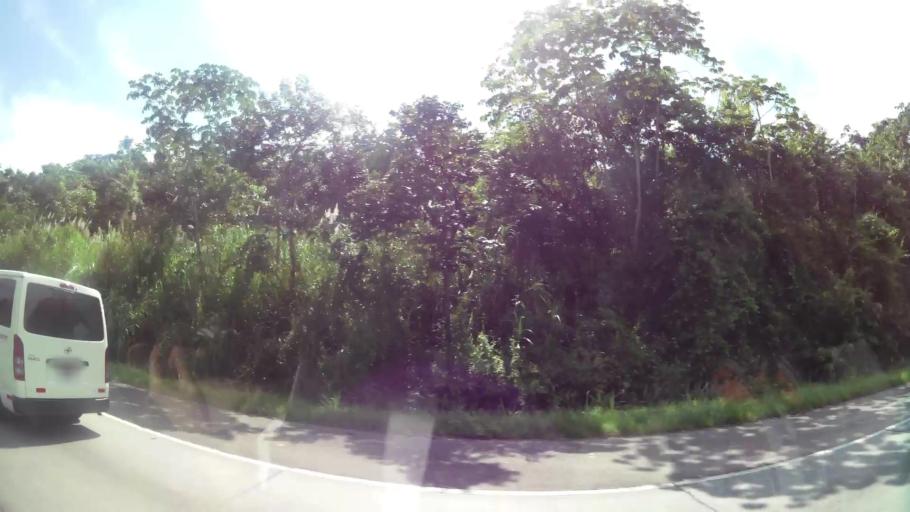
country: PA
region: Panama
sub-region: Distrito de Panama
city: Paraiso
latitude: 9.0344
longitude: -79.6168
